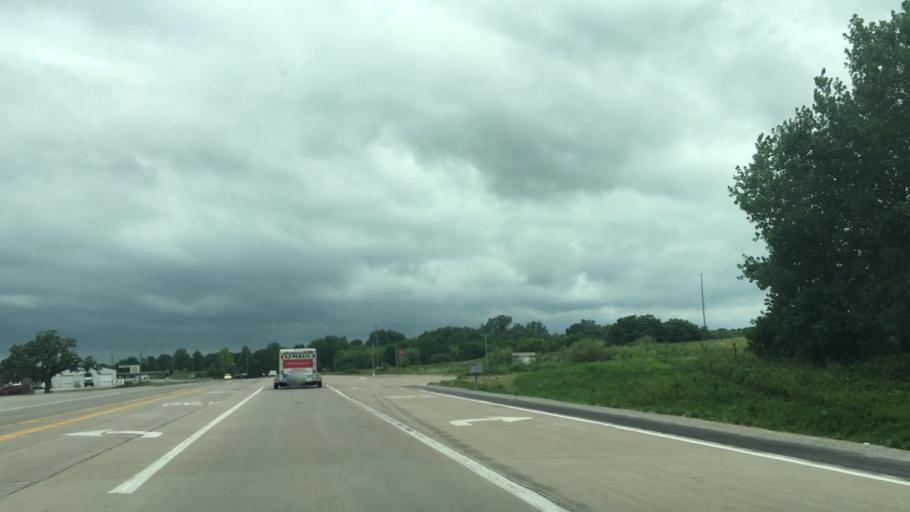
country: US
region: Iowa
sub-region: Johnson County
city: Tiffin
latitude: 41.6988
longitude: -91.6268
